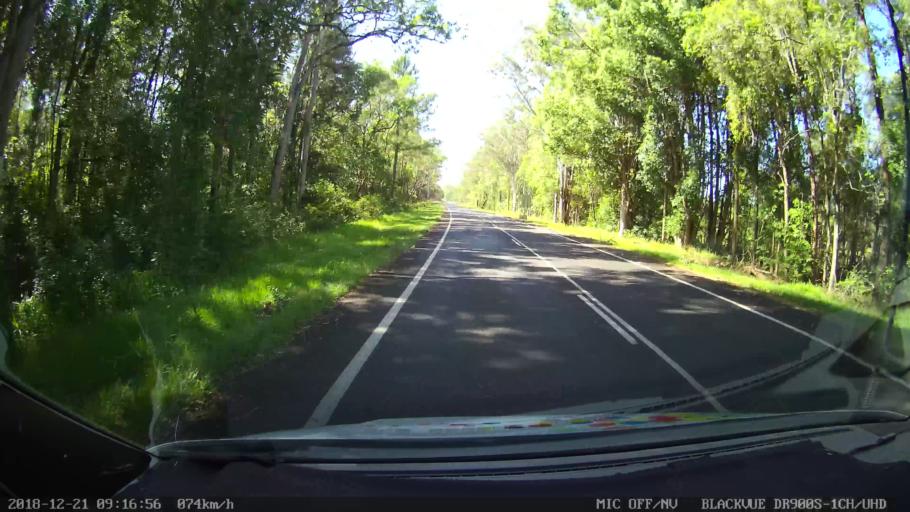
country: AU
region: New South Wales
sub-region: Clarence Valley
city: Maclean
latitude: -29.2870
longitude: 152.9889
